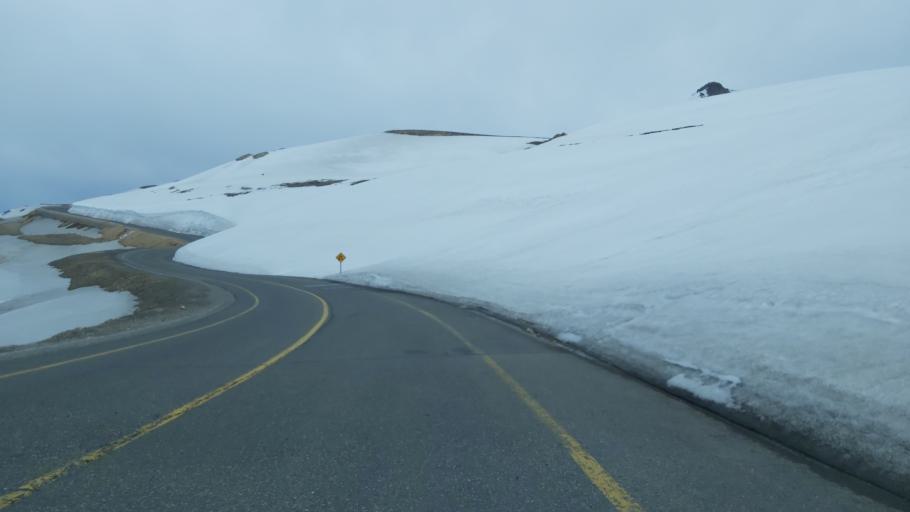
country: CL
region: Maule
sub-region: Provincia de Linares
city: Colbun
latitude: -36.0126
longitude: -70.4855
